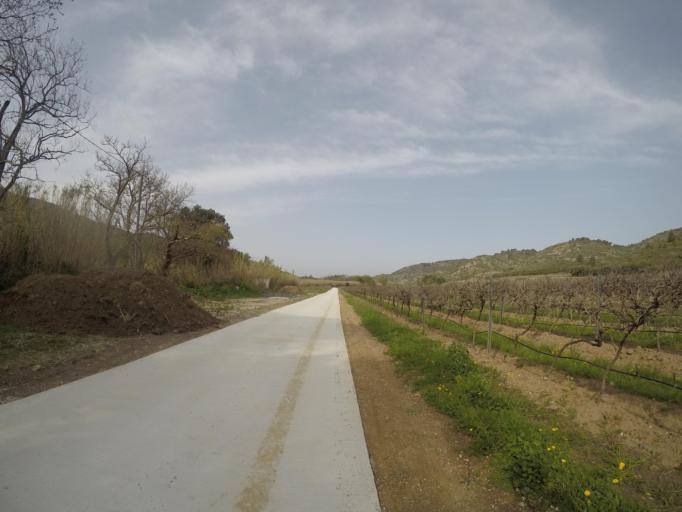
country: FR
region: Languedoc-Roussillon
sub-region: Departement des Pyrenees-Orientales
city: Estagel
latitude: 42.7771
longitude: 2.7359
